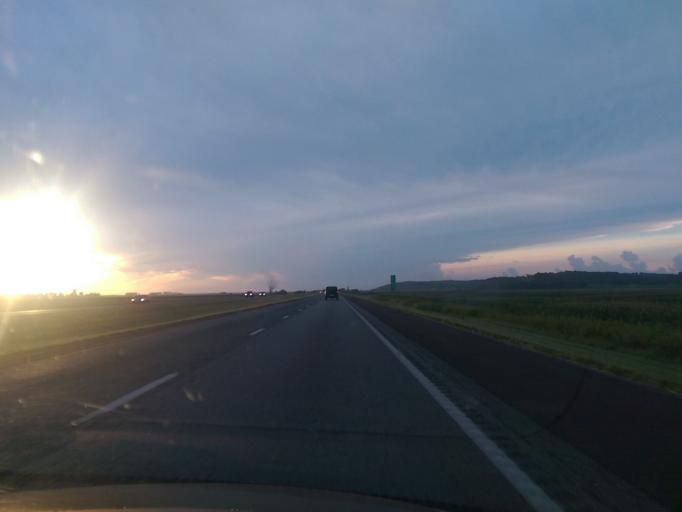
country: US
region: Missouri
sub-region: Atchison County
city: Rock Port
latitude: 40.2421
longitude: -95.4264
